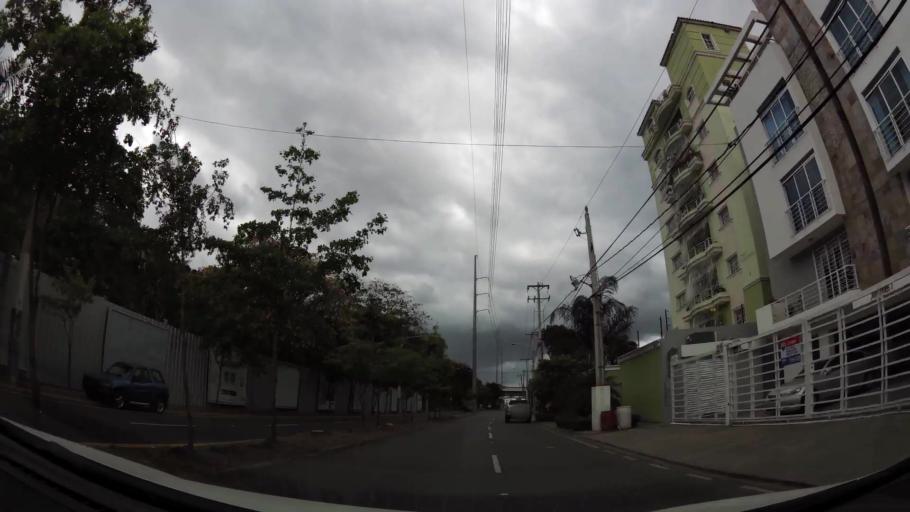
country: DO
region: Nacional
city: Bella Vista
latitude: 18.4434
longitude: -69.9488
